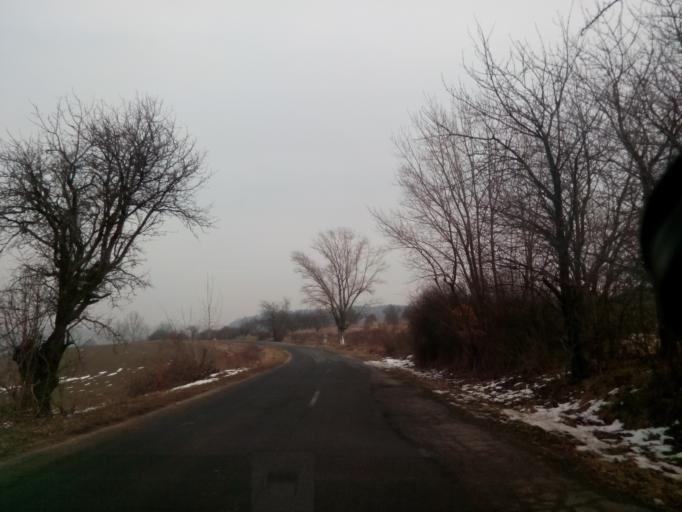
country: HU
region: Borsod-Abauj-Zemplen
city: Gonc
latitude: 48.4887
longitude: 21.2981
